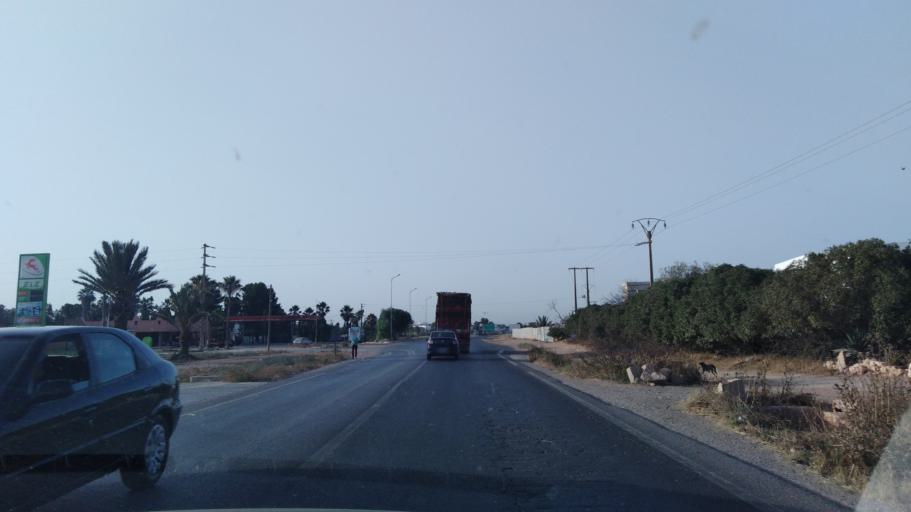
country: MA
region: Chaouia-Ouardigha
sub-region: Settat Province
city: Berrechid
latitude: 33.2356
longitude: -7.5888
